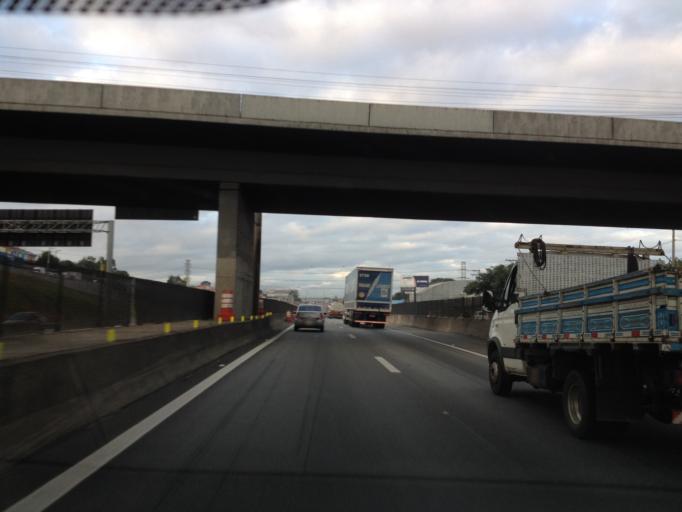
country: BR
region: Sao Paulo
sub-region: Guarulhos
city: Guarulhos
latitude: -23.4553
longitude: -46.4743
